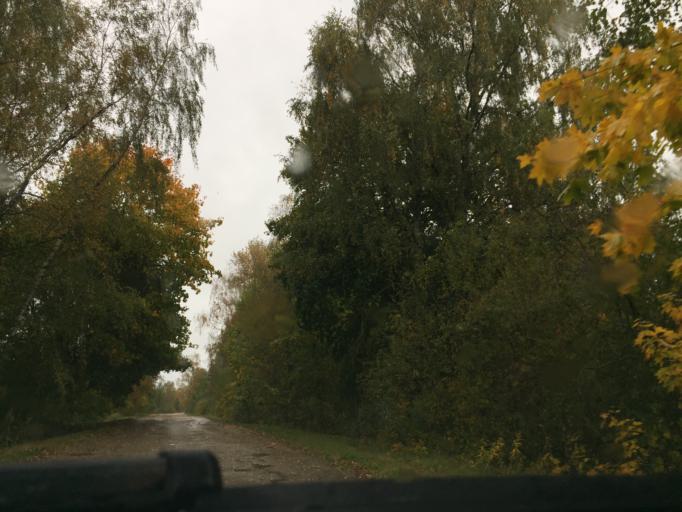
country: LV
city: Tireli
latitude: 56.8008
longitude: 23.5800
